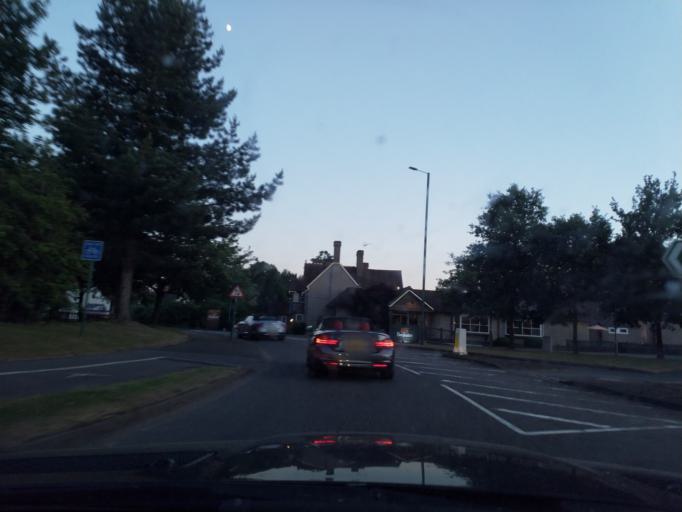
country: GB
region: England
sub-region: Solihull
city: Balsall Common
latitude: 52.4001
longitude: -1.6554
